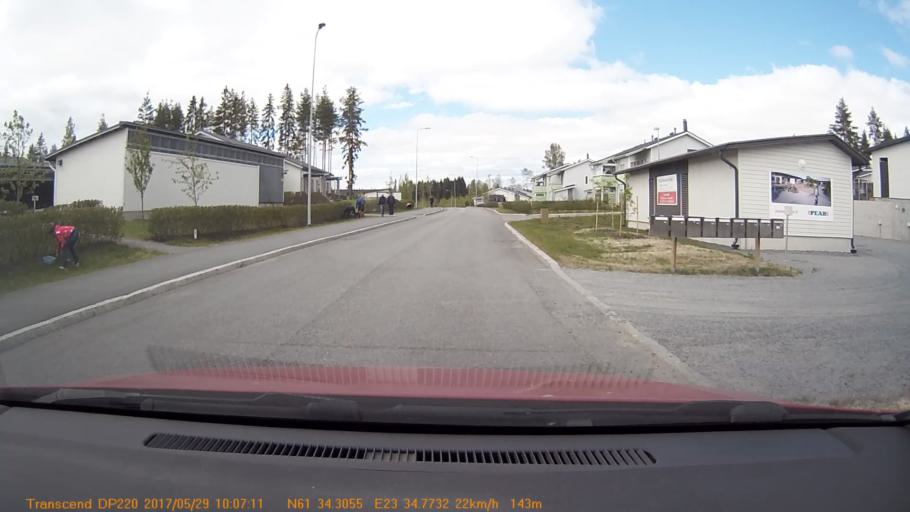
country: FI
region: Pirkanmaa
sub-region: Tampere
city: Yloejaervi
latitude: 61.5714
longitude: 23.5789
